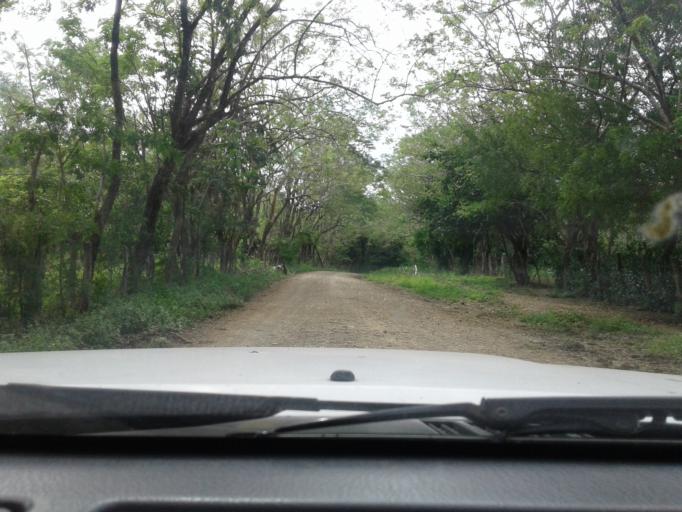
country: NI
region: Rivas
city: San Juan del Sur
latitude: 11.2134
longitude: -85.7952
